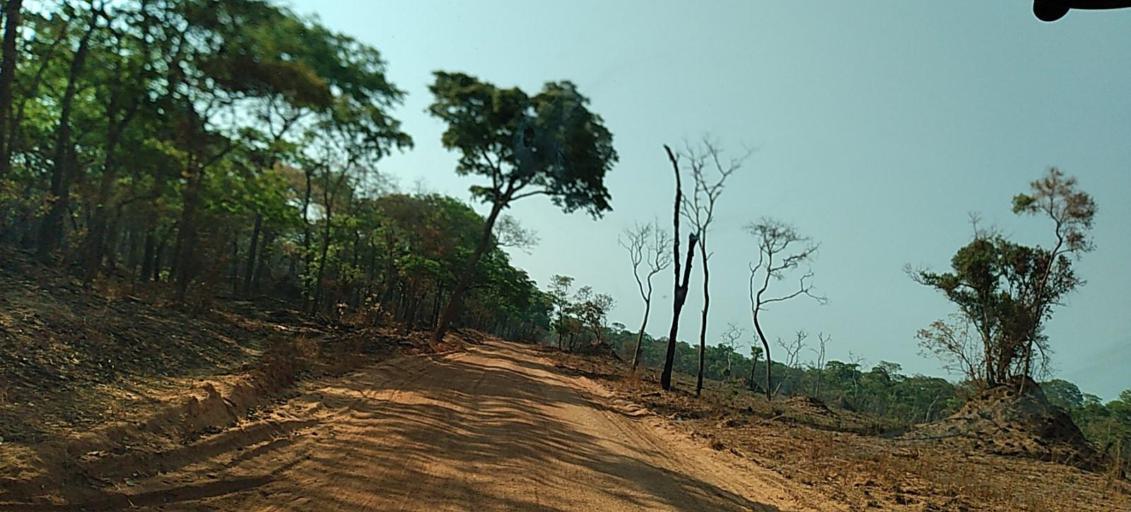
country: ZM
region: North-Western
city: Kasempa
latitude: -13.6372
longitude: 25.9937
